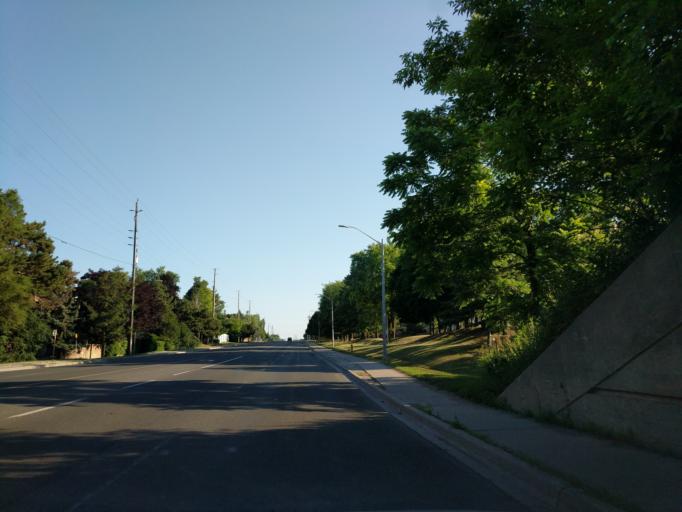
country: CA
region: Ontario
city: Willowdale
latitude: 43.8139
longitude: -79.3999
